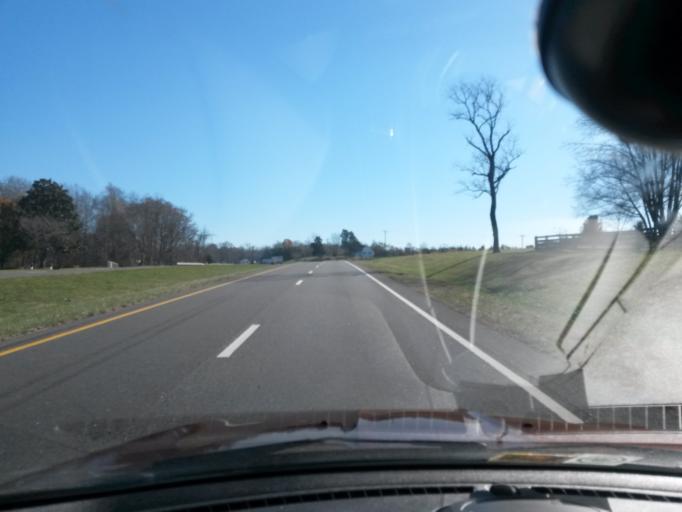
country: US
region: Virginia
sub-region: Bedford County
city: Forest
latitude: 37.3035
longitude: -79.3863
